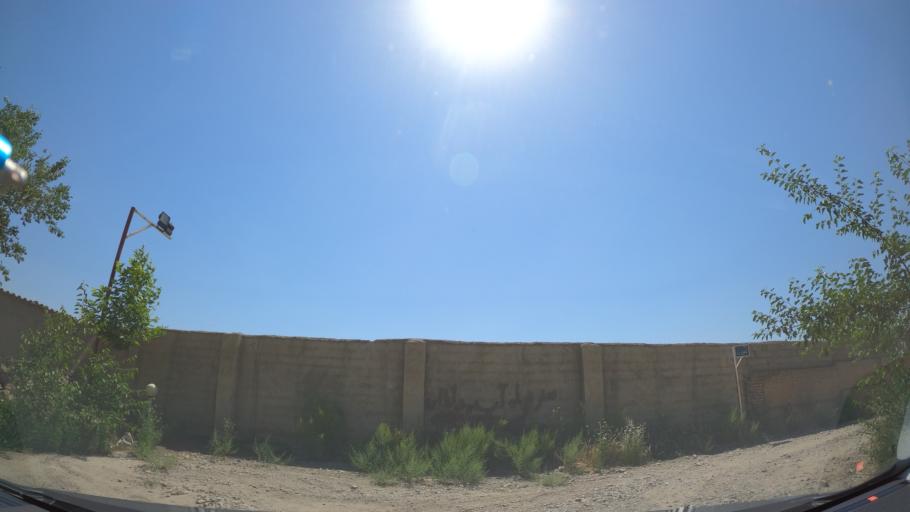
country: IR
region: Alborz
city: Hashtgerd
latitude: 35.9131
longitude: 50.7186
